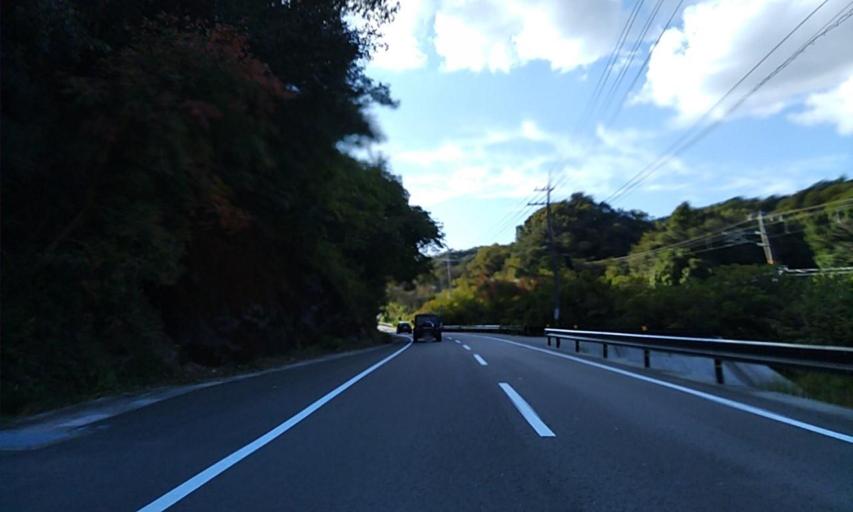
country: JP
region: Wakayama
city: Tanabe
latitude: 33.6827
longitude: 135.4031
